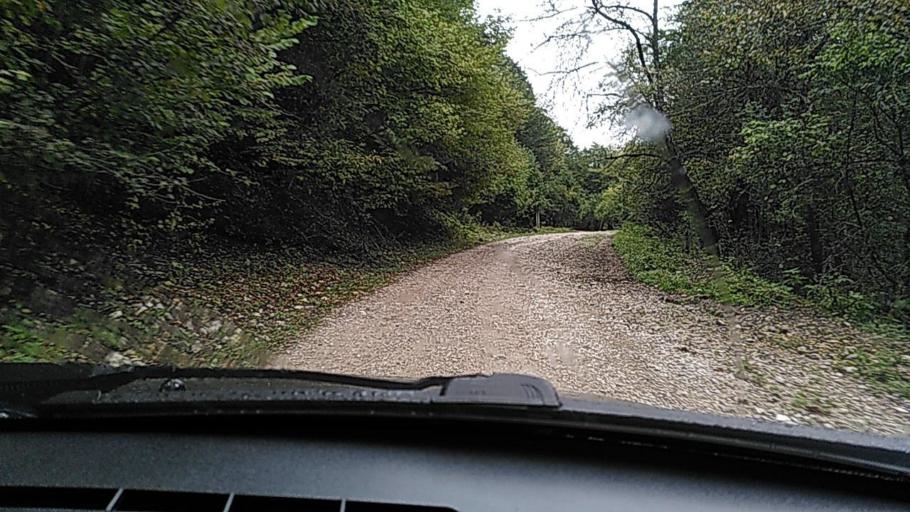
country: RU
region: Kabardino-Balkariya
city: Belaya Rechka
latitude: 43.4156
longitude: 43.4748
